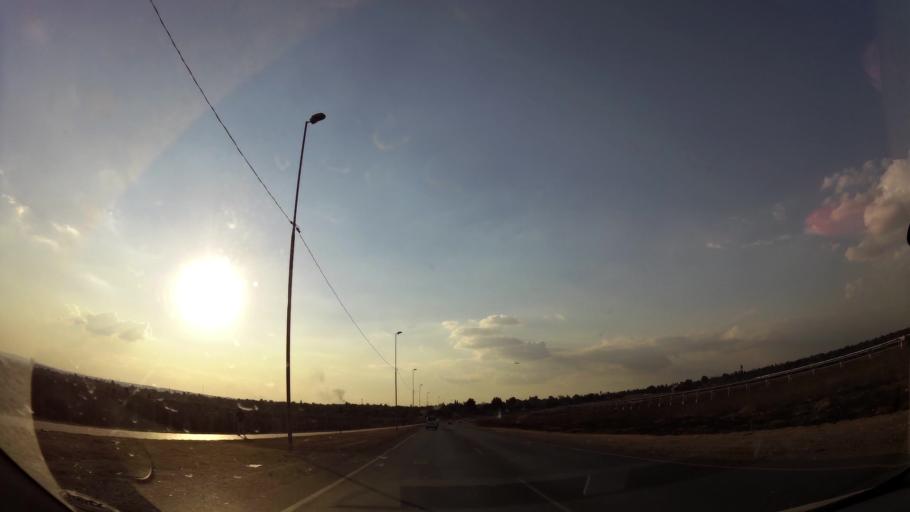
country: ZA
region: Gauteng
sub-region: Ekurhuleni Metropolitan Municipality
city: Boksburg
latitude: -26.2756
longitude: 28.2415
